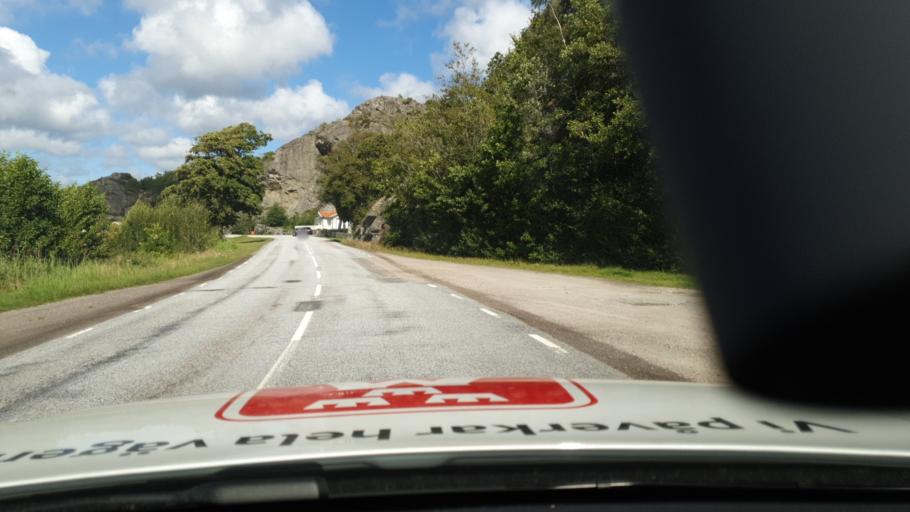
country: SE
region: Vaestra Goetaland
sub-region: Lysekils Kommun
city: Lysekil
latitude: 58.1996
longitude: 11.5369
